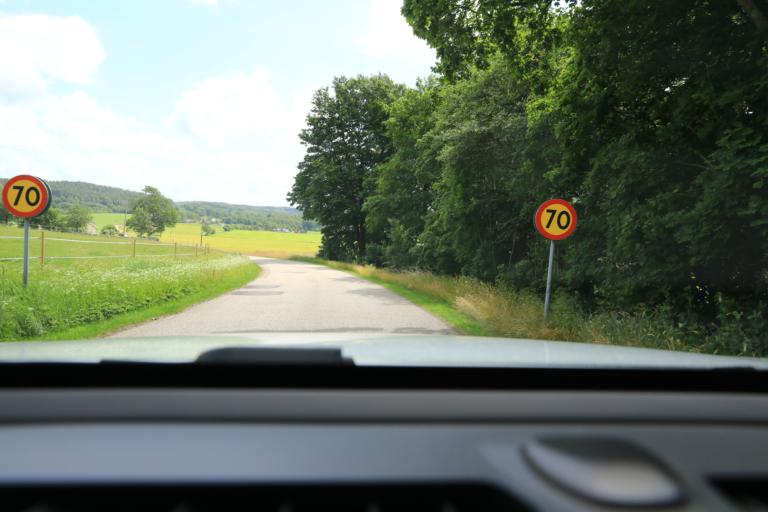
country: SE
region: Halland
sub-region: Varbergs Kommun
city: Tvaaker
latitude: 57.1119
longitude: 12.4280
